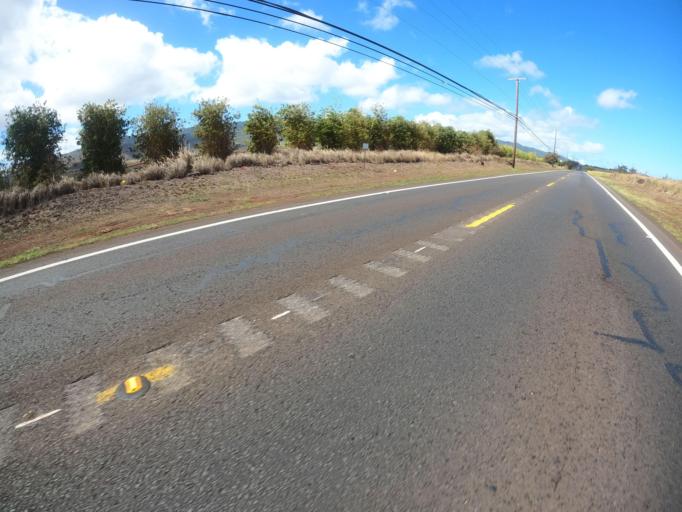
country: US
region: Hawaii
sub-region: Honolulu County
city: Village Park
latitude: 21.4037
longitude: -158.0411
